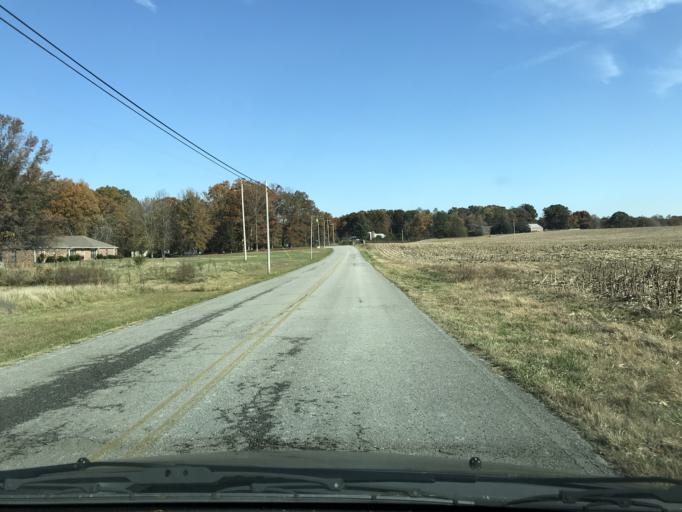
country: US
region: Tennessee
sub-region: Coffee County
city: Tullahoma
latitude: 35.4043
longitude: -86.1571
